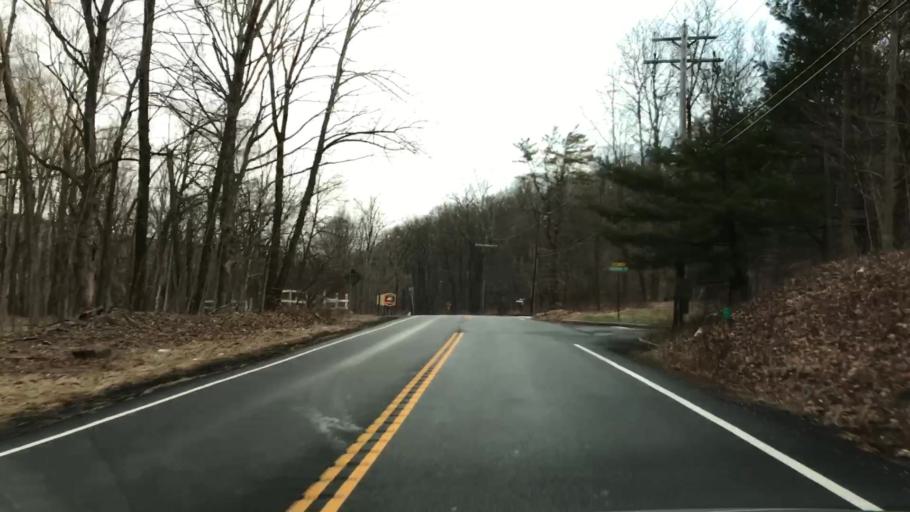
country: US
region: New York
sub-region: Rockland County
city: Wesley Hills
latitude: 41.1717
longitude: -74.0839
